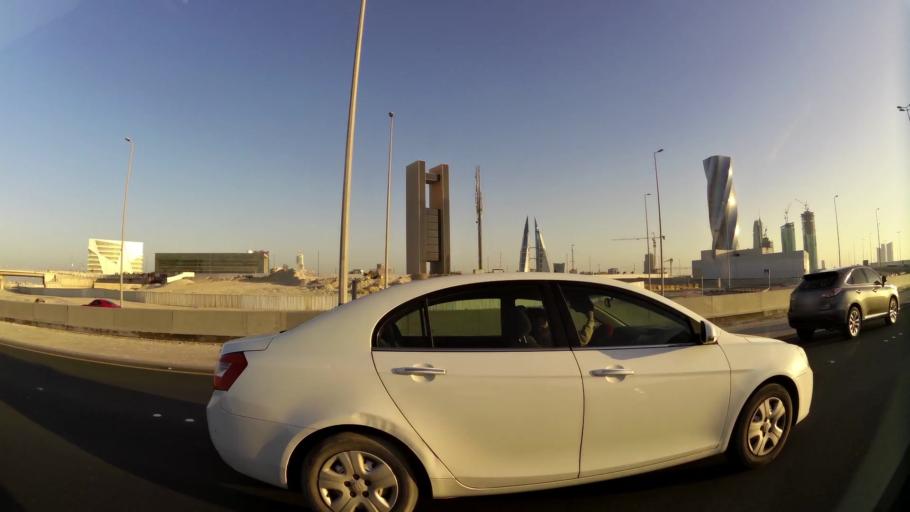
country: BH
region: Muharraq
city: Al Muharraq
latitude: 26.2530
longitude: 50.5789
